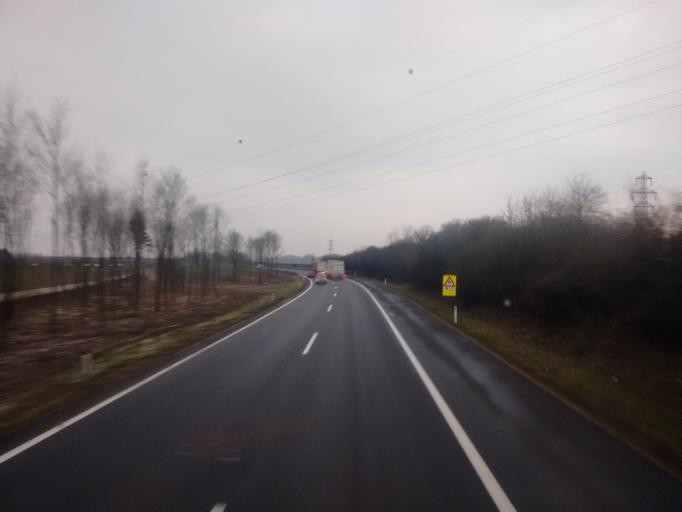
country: AT
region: Upper Austria
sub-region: Wels Stadt
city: Wels
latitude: 48.1815
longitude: 14.0017
